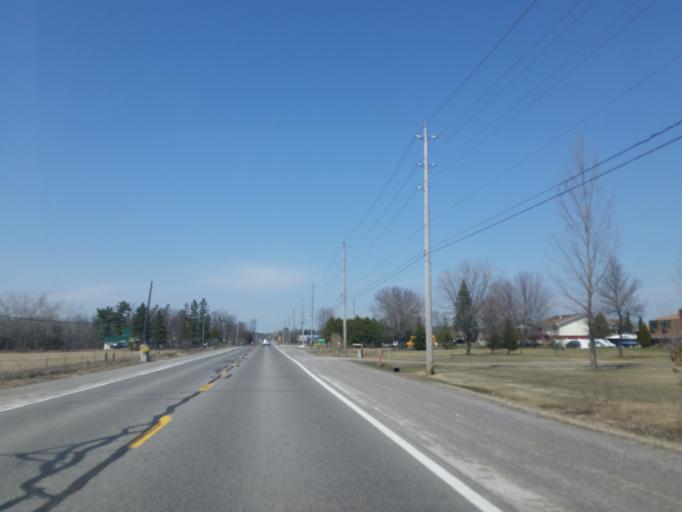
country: CA
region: Ontario
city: Bells Corners
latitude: 45.4547
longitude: -76.0652
